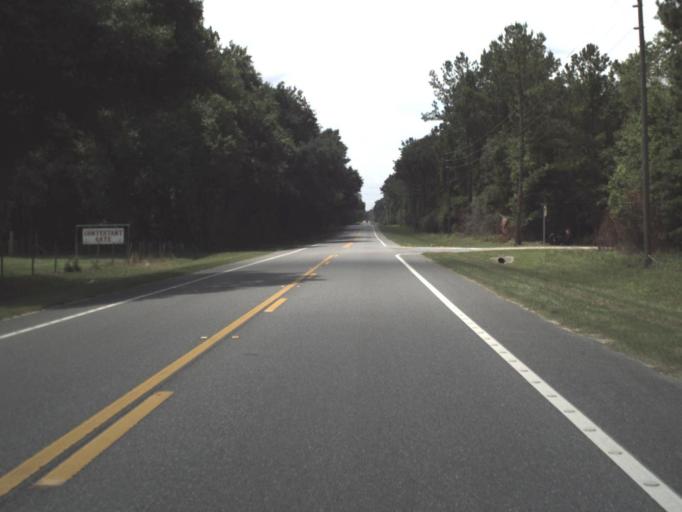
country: US
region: Florida
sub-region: Lafayette County
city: Mayo
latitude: 29.9856
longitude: -82.9345
